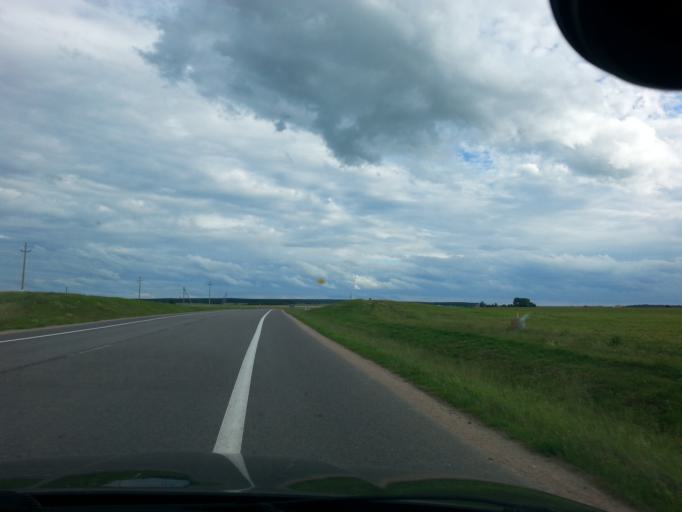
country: BY
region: Grodnenskaya
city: Astravyets
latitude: 54.7389
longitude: 26.0871
